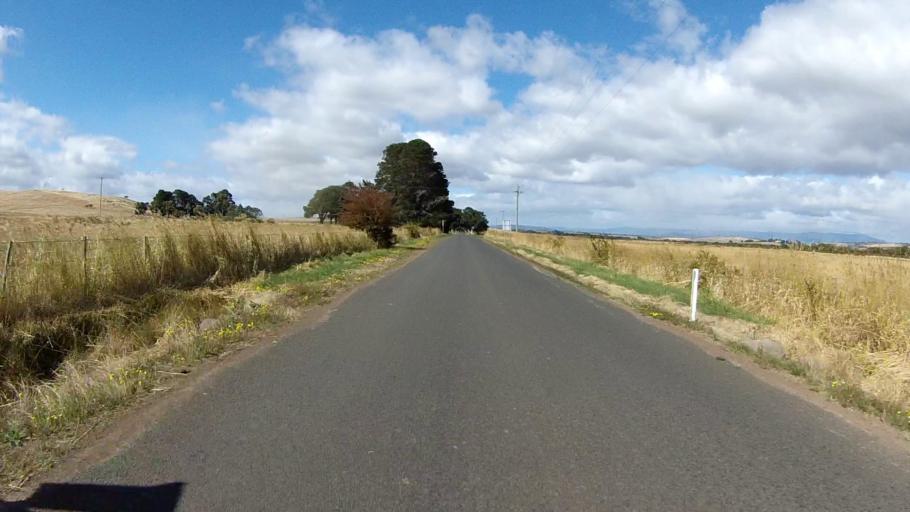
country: AU
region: Tasmania
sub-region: Northern Midlands
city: Evandale
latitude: -41.7495
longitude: 147.4886
